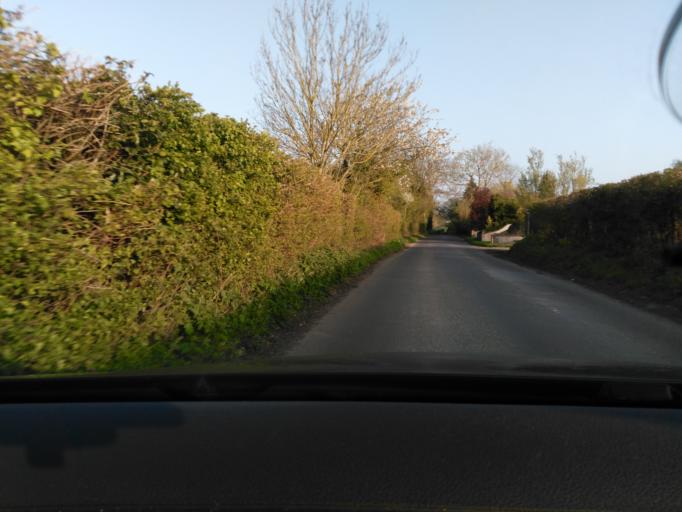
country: GB
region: England
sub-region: Hampshire
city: Tadley
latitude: 51.3496
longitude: -1.0925
